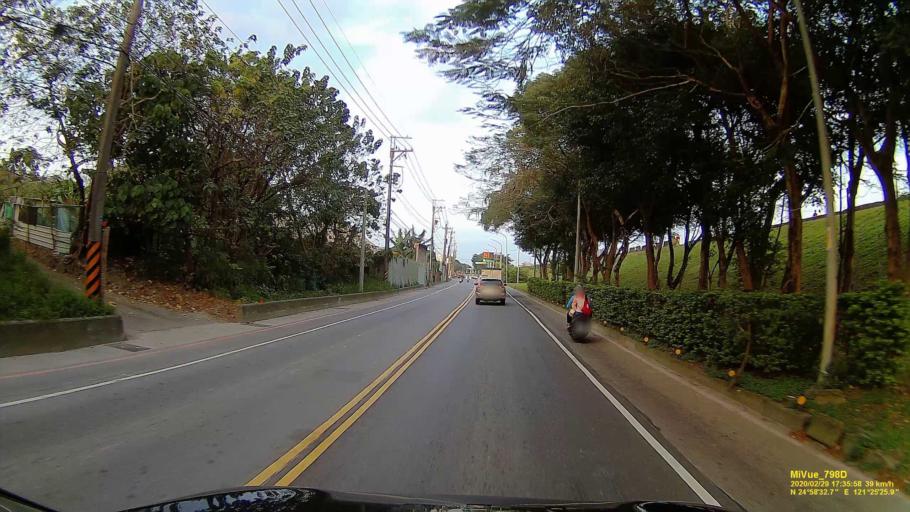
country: TW
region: Taipei
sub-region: Taipei
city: Banqiao
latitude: 24.9759
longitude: 121.4241
